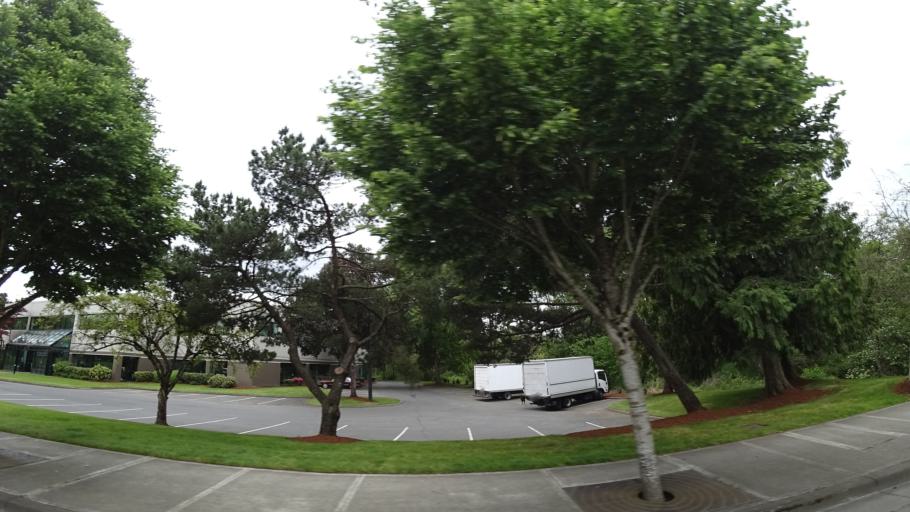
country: US
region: Oregon
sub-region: Washington County
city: Beaverton
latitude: 45.4608
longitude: -122.7946
